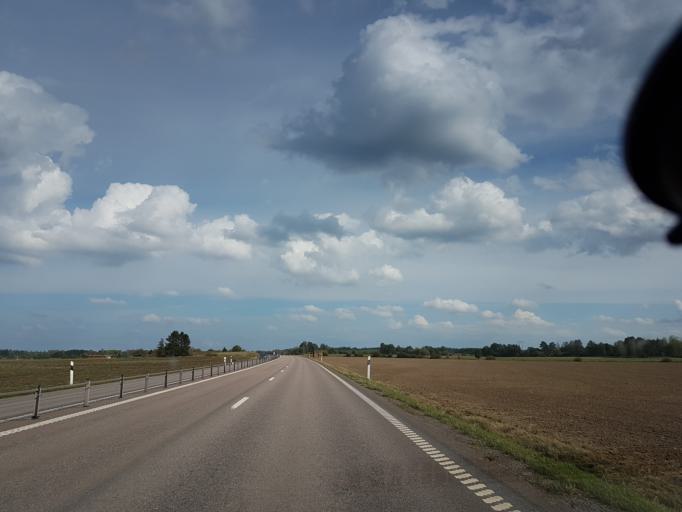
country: SE
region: OEstergoetland
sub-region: Linkopings Kommun
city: Malmslatt
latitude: 58.3758
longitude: 15.5047
